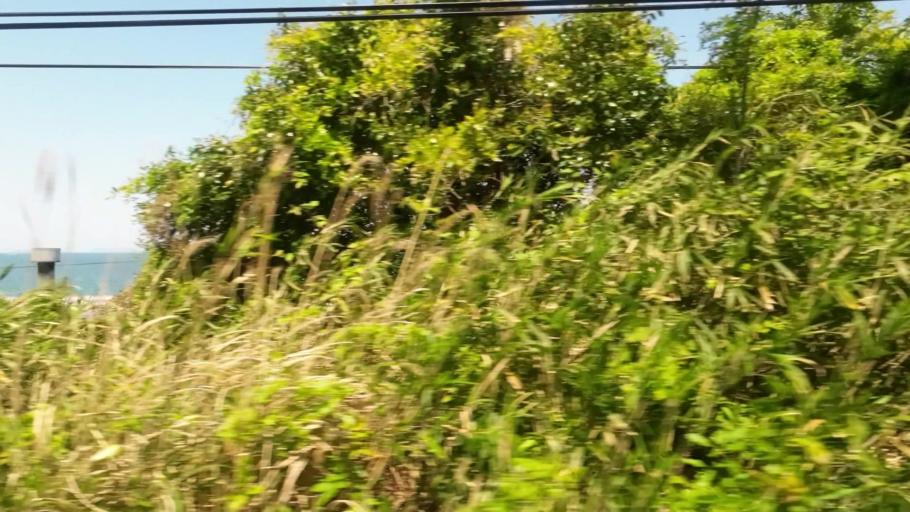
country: JP
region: Ehime
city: Hojo
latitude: 34.0291
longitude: 132.8284
